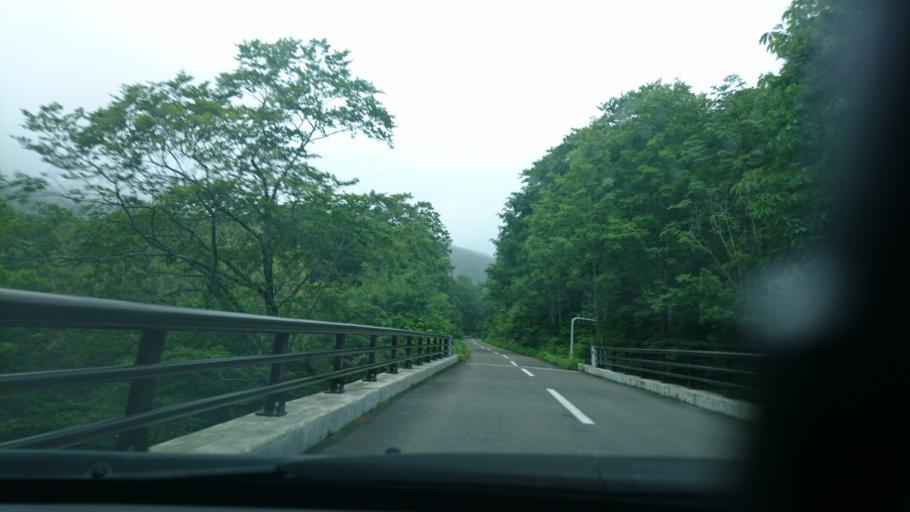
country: JP
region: Akita
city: Yuzawa
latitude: 39.1431
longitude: 140.7686
